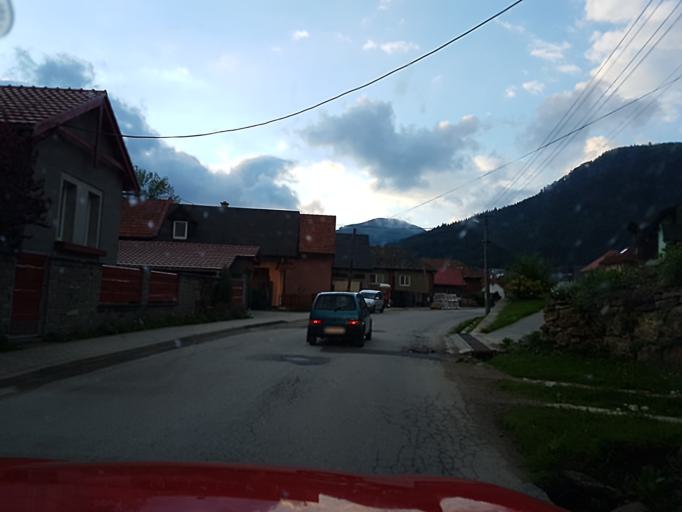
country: SK
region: Zilinsky
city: Ruzomberok
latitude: 49.1258
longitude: 19.4053
